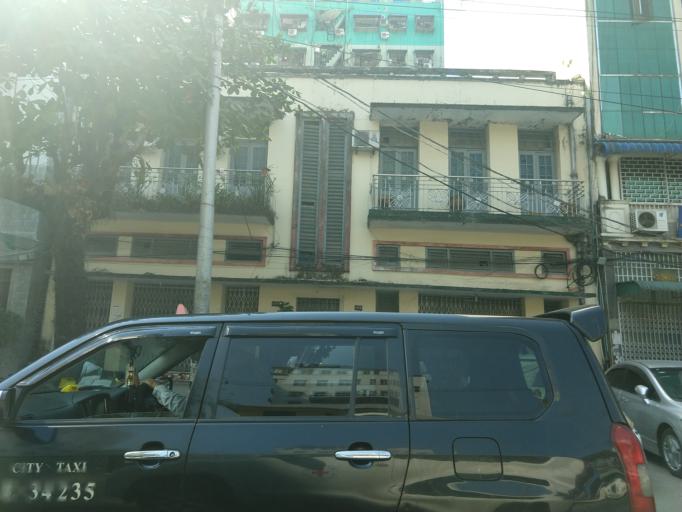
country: MM
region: Yangon
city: Yangon
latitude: 16.7724
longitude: 96.1725
